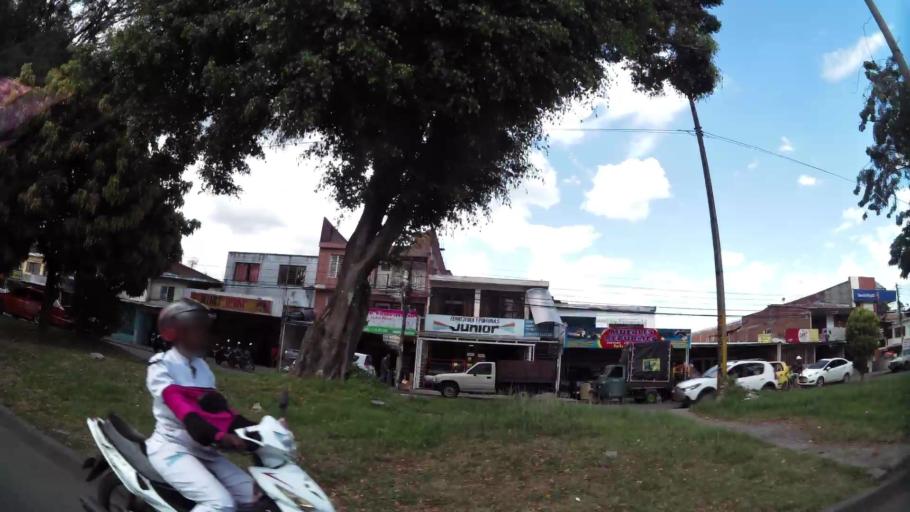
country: CO
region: Valle del Cauca
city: Cali
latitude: 3.4081
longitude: -76.5167
